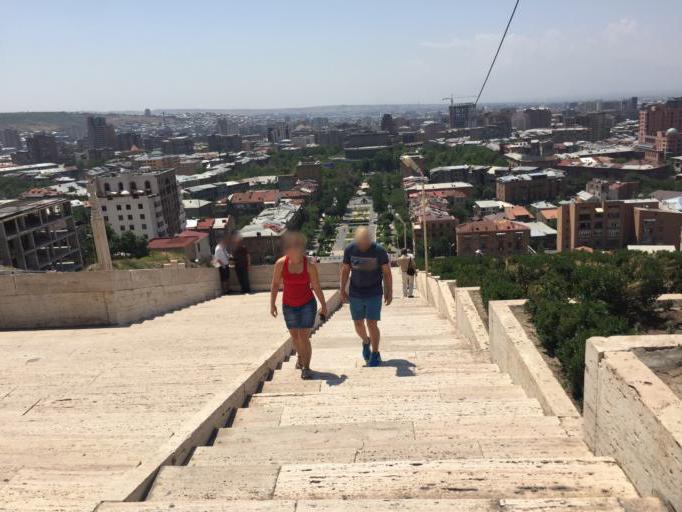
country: AM
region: Yerevan
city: Yerevan
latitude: 40.1925
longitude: 44.5155
